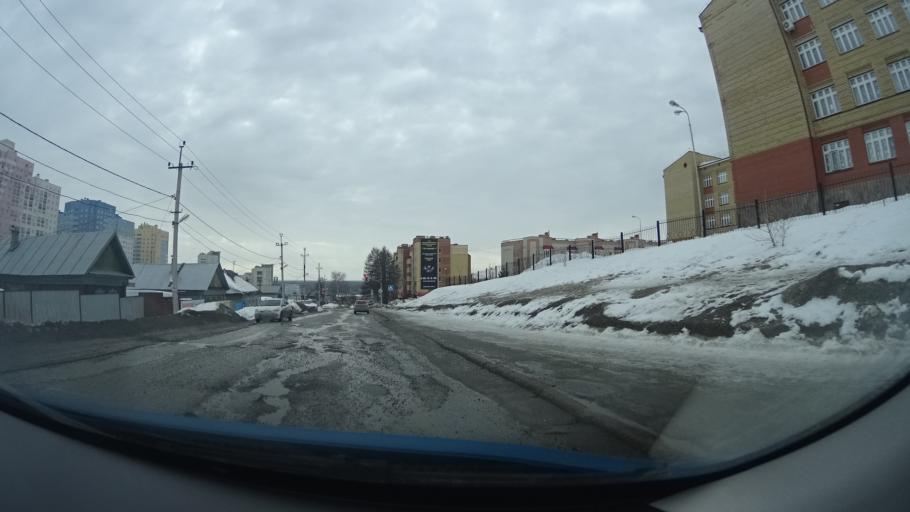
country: RU
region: Bashkortostan
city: Ufa
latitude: 54.6942
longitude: 55.9884
